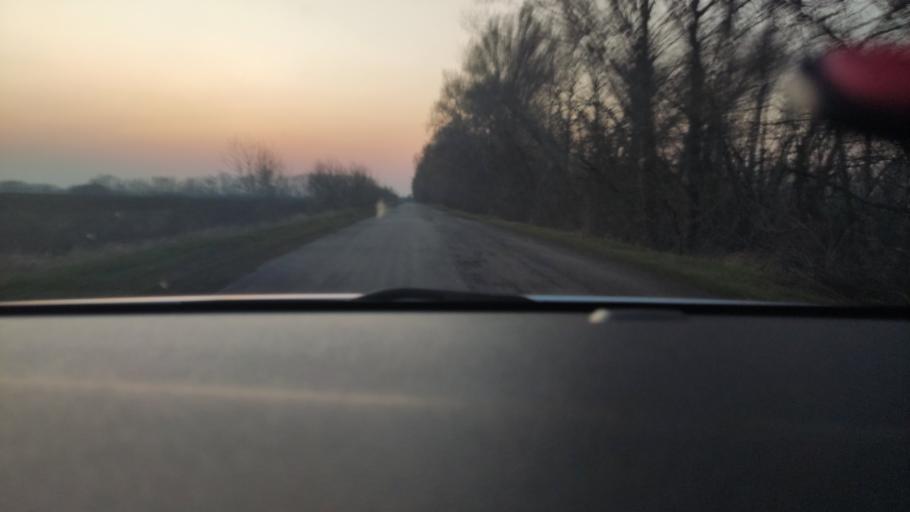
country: RU
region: Voronezj
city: Uryv-Pokrovka
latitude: 51.1304
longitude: 39.1018
